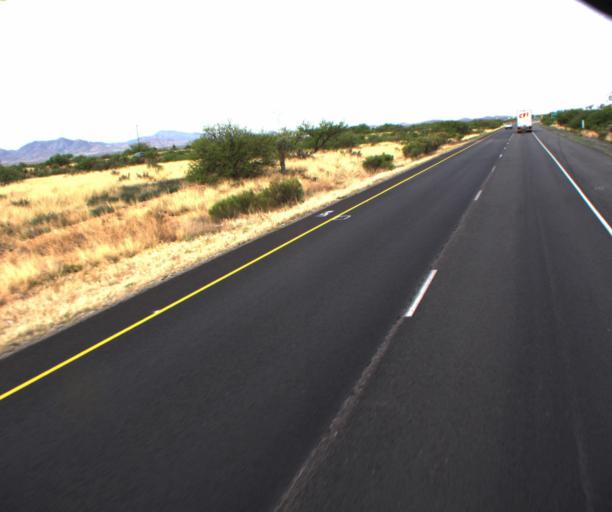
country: US
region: Arizona
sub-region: Cochise County
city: Mescal
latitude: 31.9751
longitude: -110.5028
